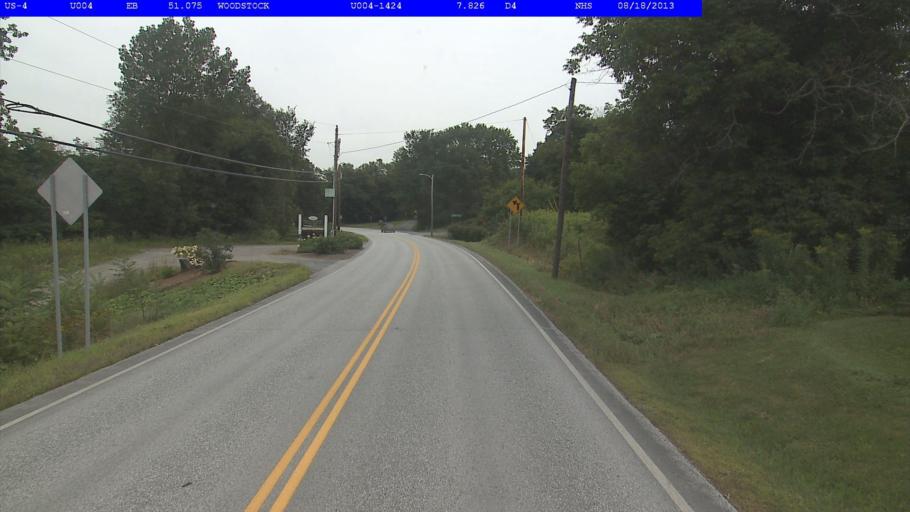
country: US
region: Vermont
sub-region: Windsor County
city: Woodstock
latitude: 43.6361
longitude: -72.4960
